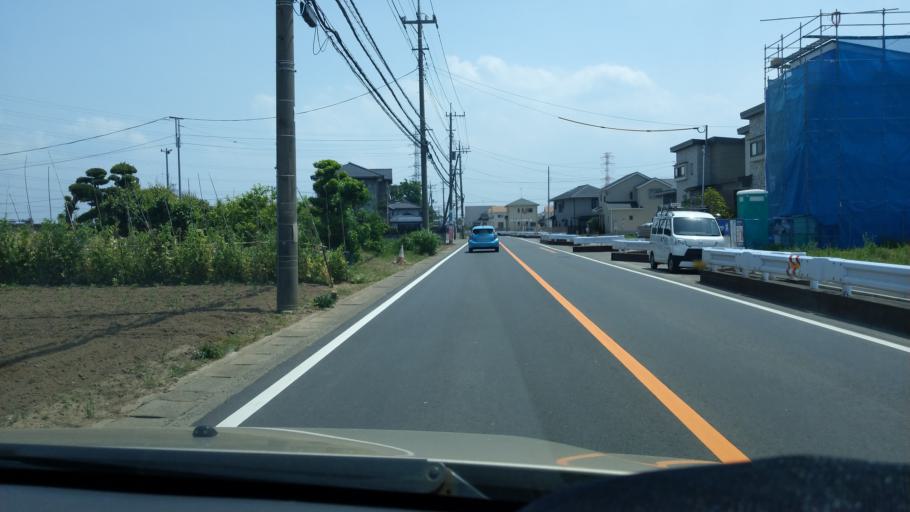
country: JP
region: Saitama
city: Koshigaya
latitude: 35.9046
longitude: 139.7322
